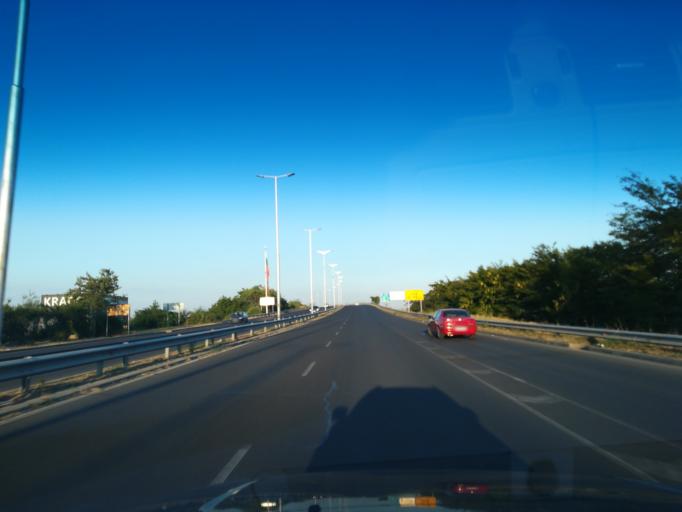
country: BG
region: Plovdiv
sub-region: Obshtina Plovdiv
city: Plovdiv
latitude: 42.1482
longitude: 24.8009
